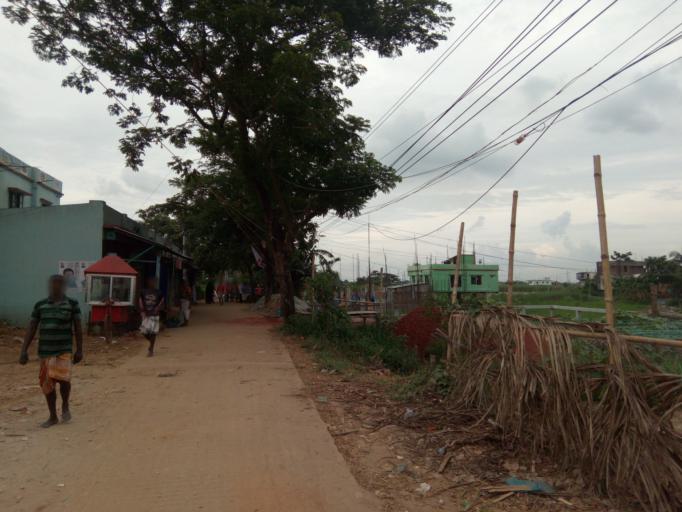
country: BD
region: Dhaka
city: Paltan
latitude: 23.7377
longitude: 90.4538
